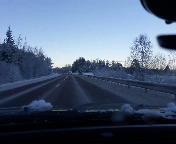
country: SE
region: Gaevleborg
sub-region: Ljusdals Kommun
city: Ljusdal
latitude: 61.8026
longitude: 16.1119
